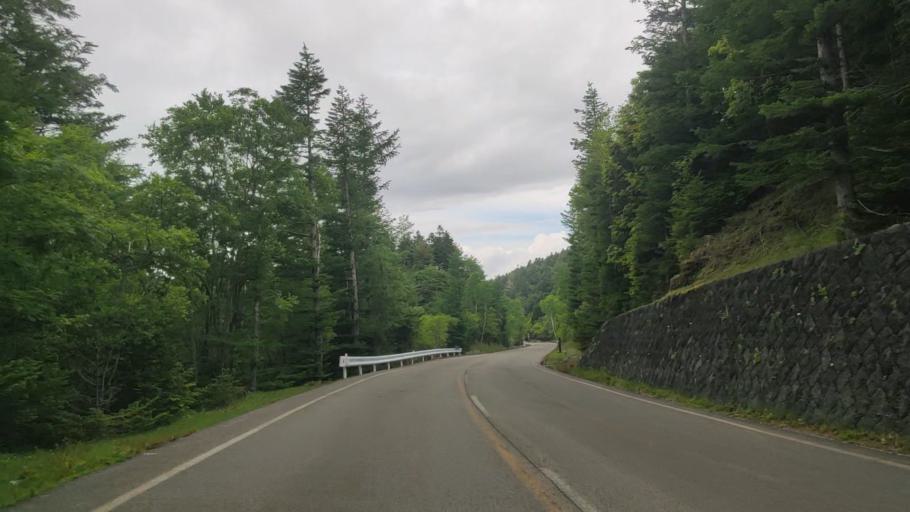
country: JP
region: Yamanashi
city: Fujikawaguchiko
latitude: 35.3808
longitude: 138.6904
